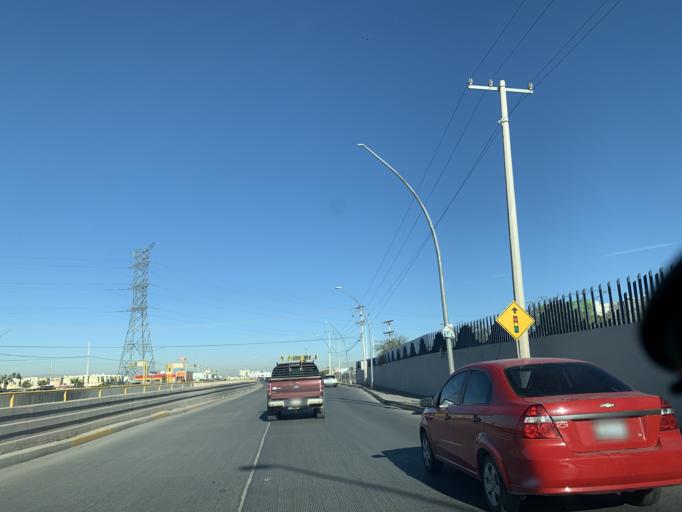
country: US
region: Texas
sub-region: El Paso County
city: Socorro
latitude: 31.6737
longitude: -106.3863
